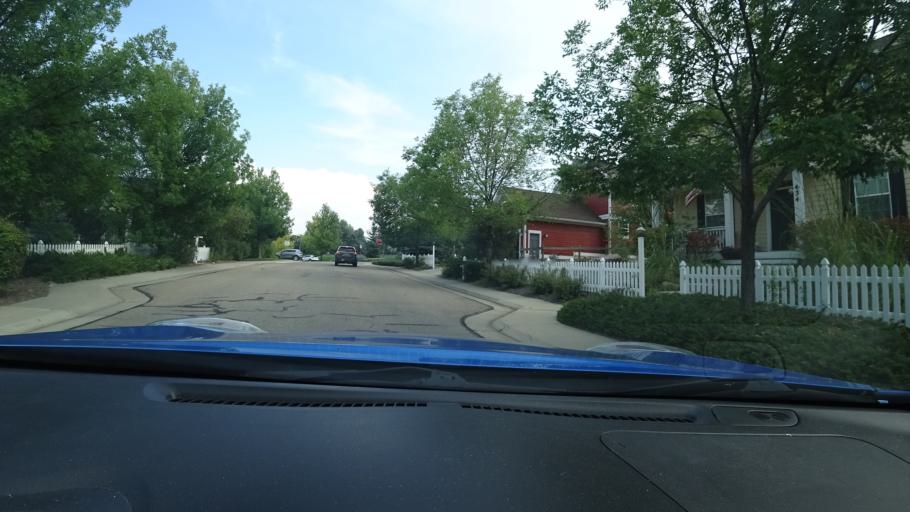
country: US
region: Colorado
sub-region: Boulder County
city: Louisville
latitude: 40.0007
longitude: -105.1377
